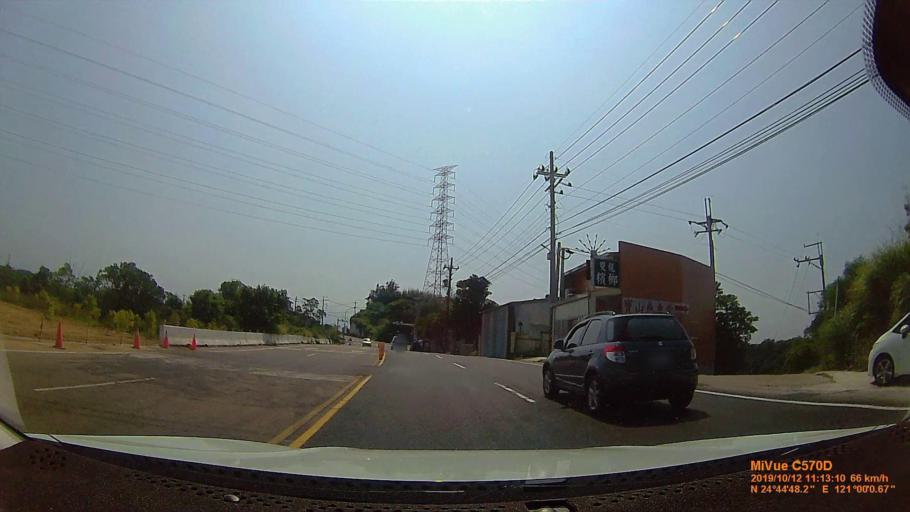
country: TW
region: Taiwan
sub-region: Hsinchu
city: Hsinchu
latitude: 24.7466
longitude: 121.0002
